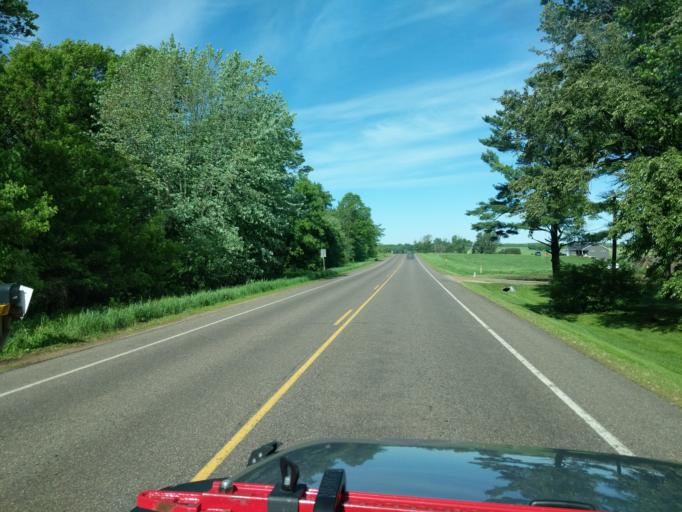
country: US
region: Wisconsin
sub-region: Pierce County
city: River Falls
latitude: 44.8697
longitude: -92.4996
